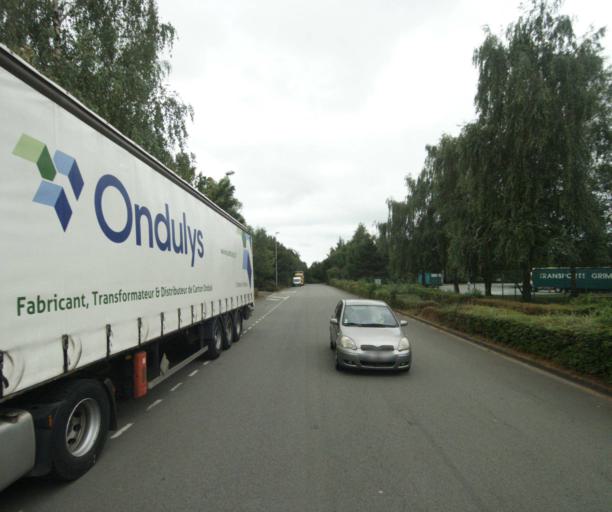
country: FR
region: Nord-Pas-de-Calais
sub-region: Departement du Nord
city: Fretin
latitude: 50.5737
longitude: 3.1395
